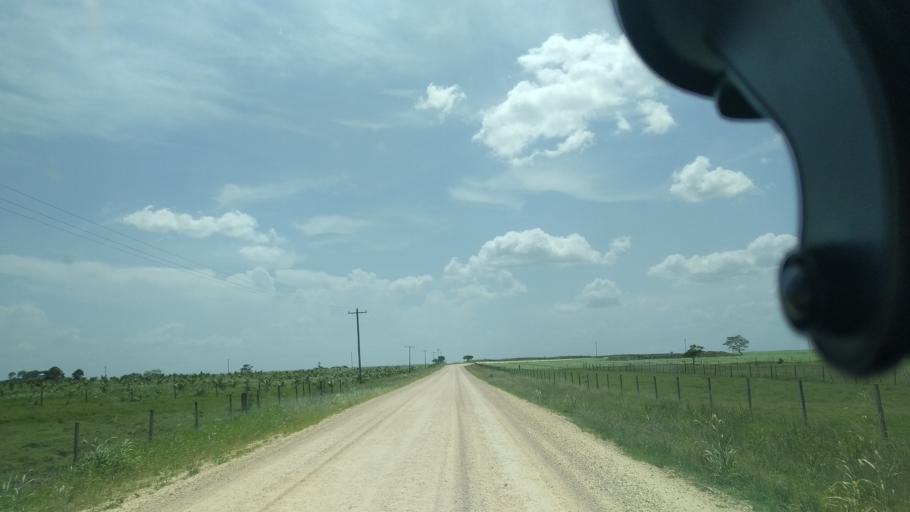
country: BZ
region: Cayo
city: San Ignacio
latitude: 17.3148
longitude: -89.0437
